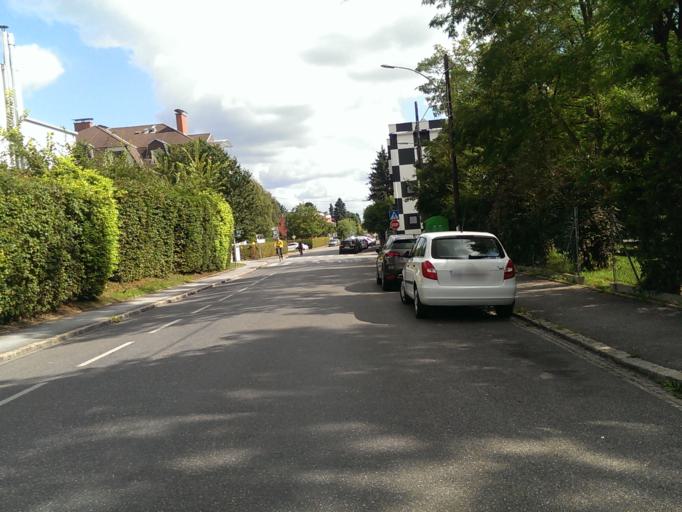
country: AT
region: Styria
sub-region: Graz Stadt
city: Graz
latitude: 47.0518
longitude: 15.4584
